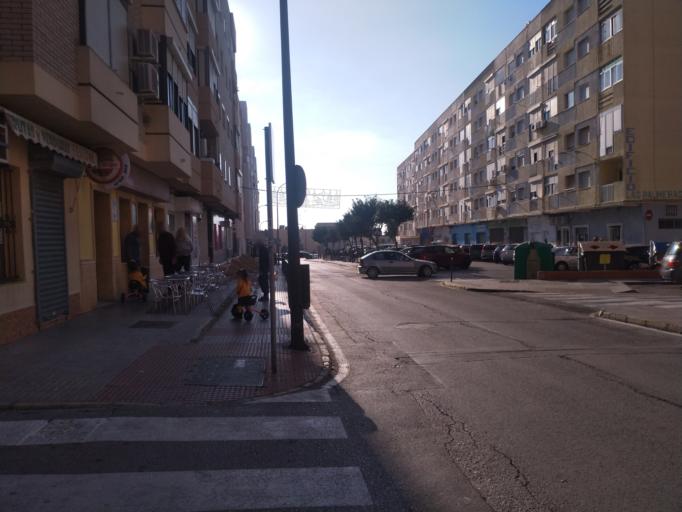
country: ES
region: Andalusia
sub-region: Provincia de Cadiz
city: San Fernando
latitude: 36.4558
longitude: -6.2086
